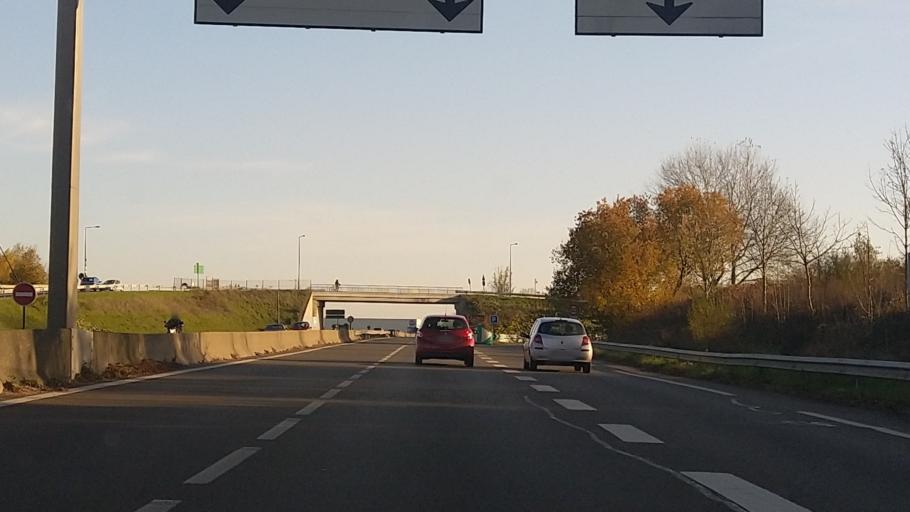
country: FR
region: Ile-de-France
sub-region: Departement du Val-d'Oise
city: Moisselles
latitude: 49.0448
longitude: 2.3364
